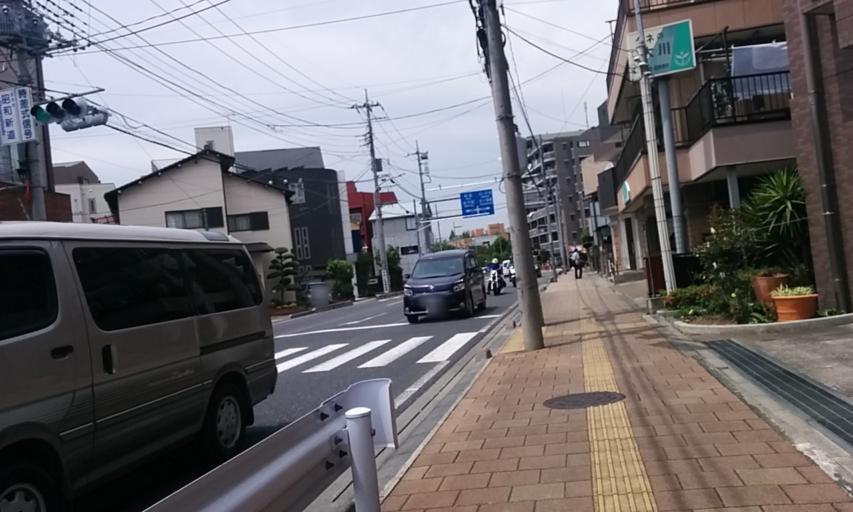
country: JP
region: Saitama
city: Shiki
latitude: 35.8295
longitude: 139.5794
